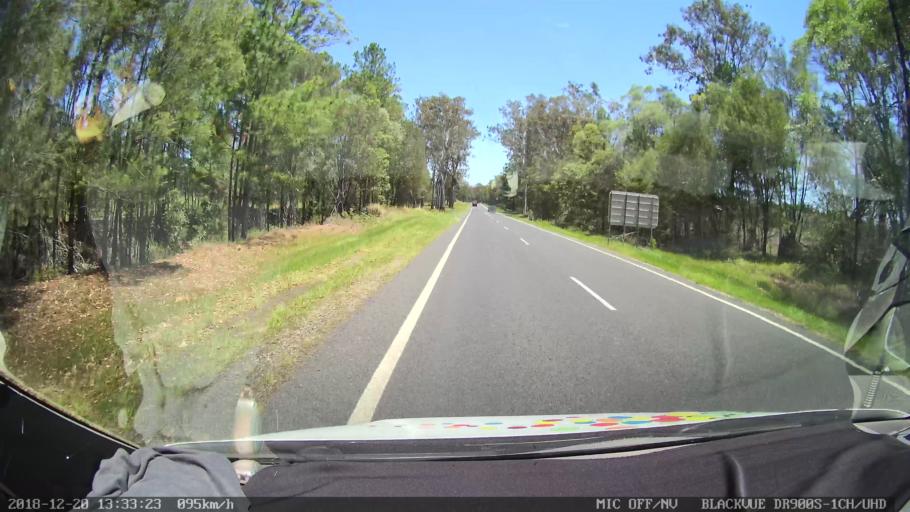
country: AU
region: New South Wales
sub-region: Clarence Valley
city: Gordon
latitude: -29.2446
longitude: 152.9867
